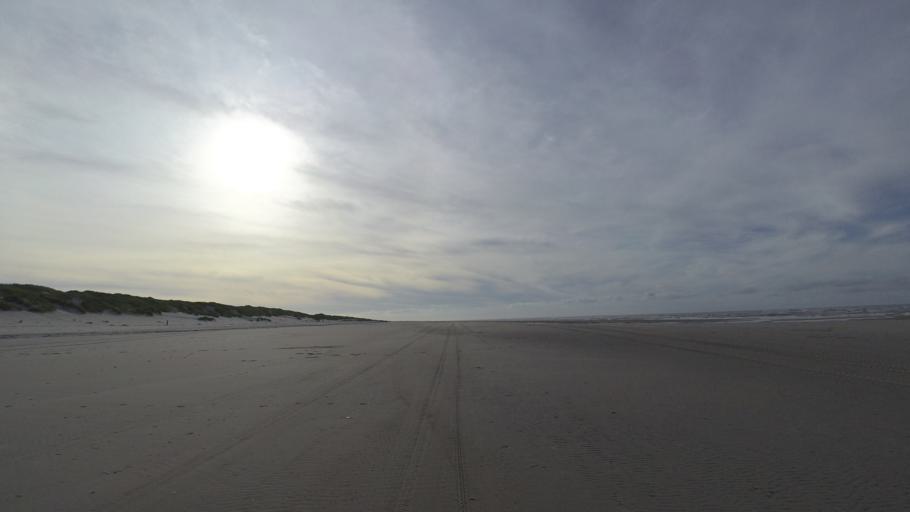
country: NL
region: Friesland
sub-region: Gemeente Ameland
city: Nes
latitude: 53.4644
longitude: 5.8448
